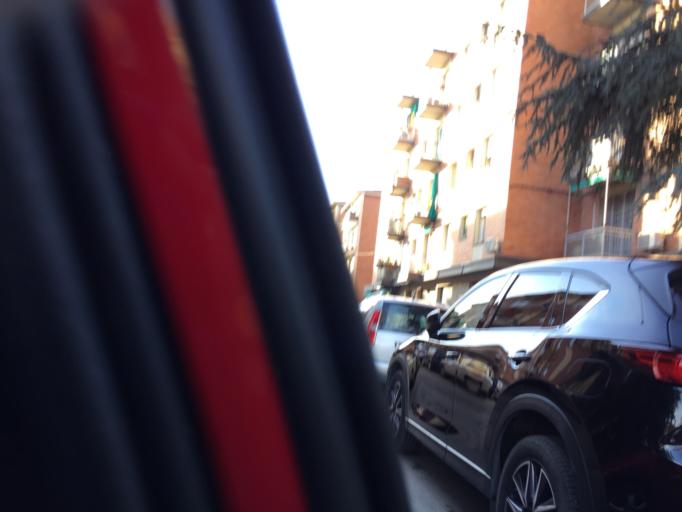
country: IT
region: Emilia-Romagna
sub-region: Provincia di Bologna
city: Casalecchio di Reno
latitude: 44.4986
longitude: 11.2930
